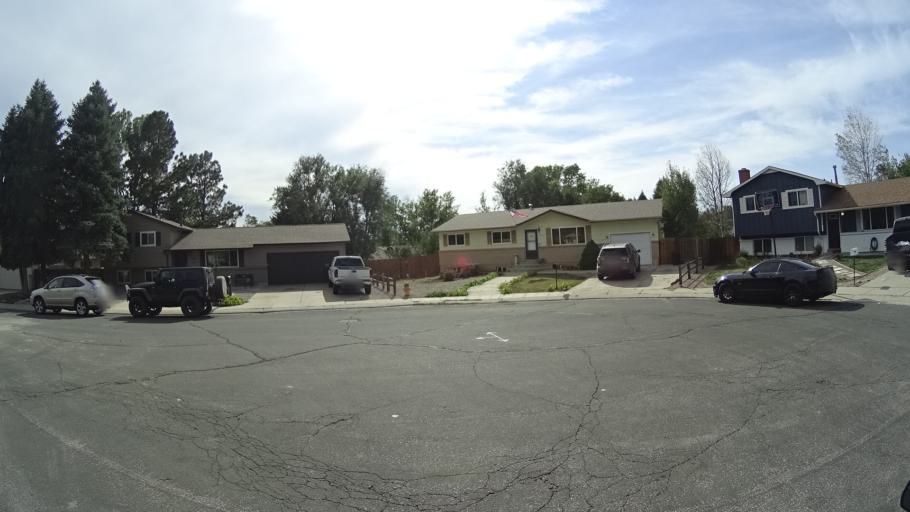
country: US
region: Colorado
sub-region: El Paso County
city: Cimarron Hills
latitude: 38.8975
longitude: -104.7667
